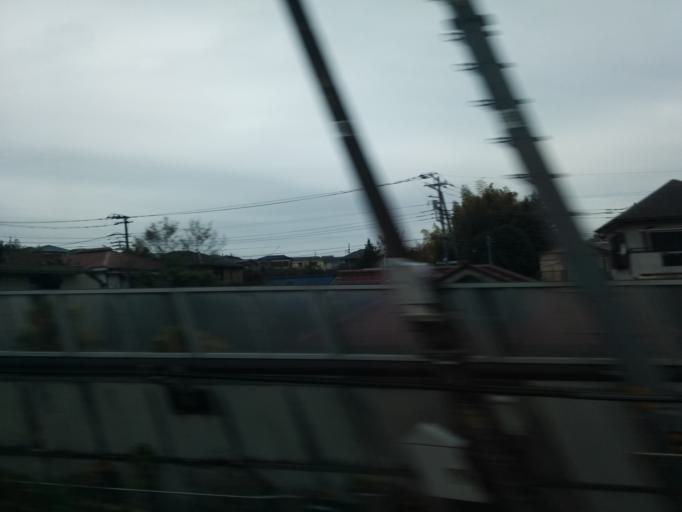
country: JP
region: Kanagawa
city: Yokohama
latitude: 35.4737
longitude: 139.5572
